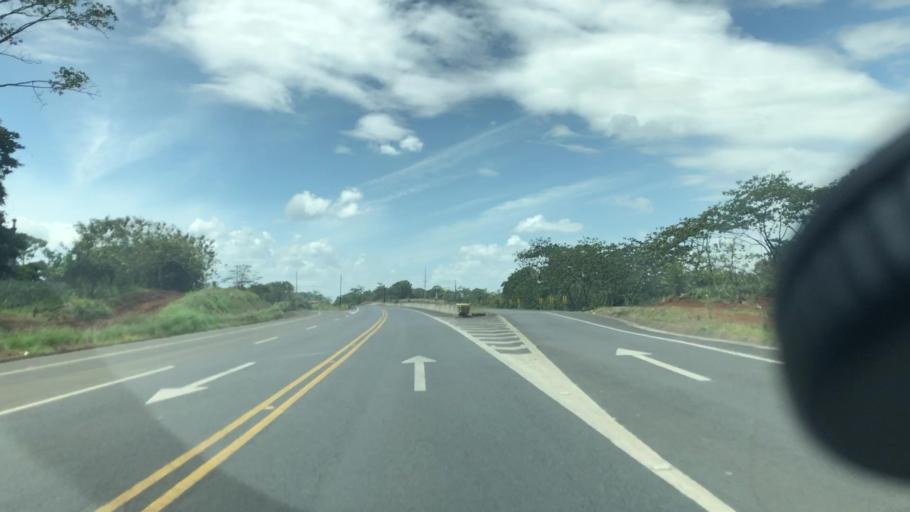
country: CR
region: Heredia
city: La Virgen
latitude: 10.4408
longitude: -84.1569
